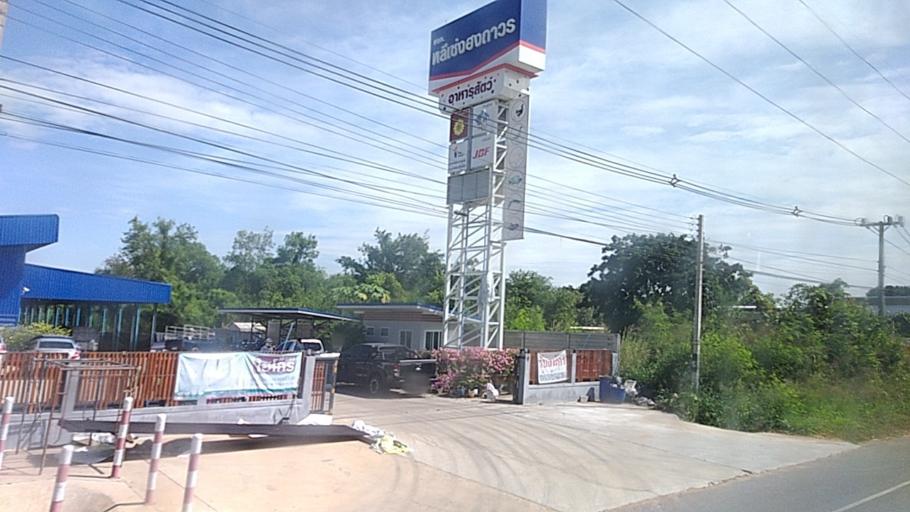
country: TH
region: Maha Sarakham
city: Chiang Yuen
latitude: 16.4425
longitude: 102.9703
